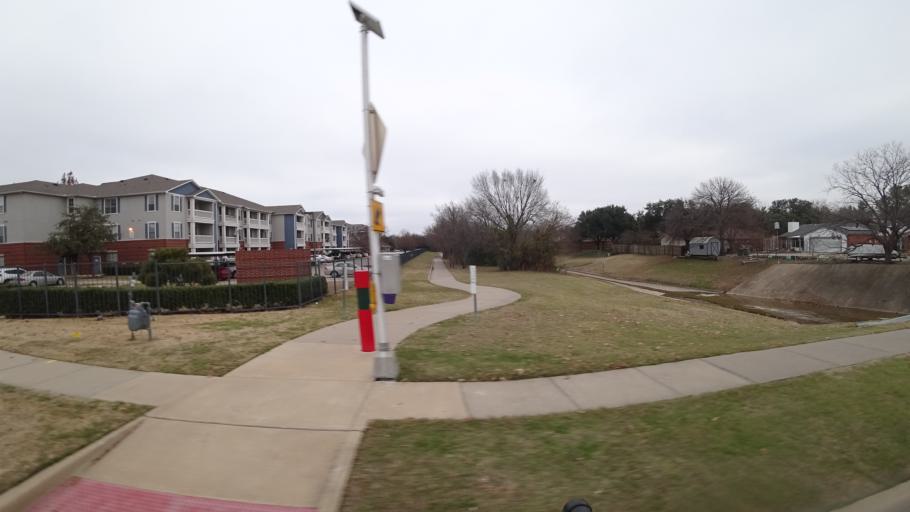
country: US
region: Texas
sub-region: Denton County
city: Highland Village
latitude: 33.0535
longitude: -97.0353
